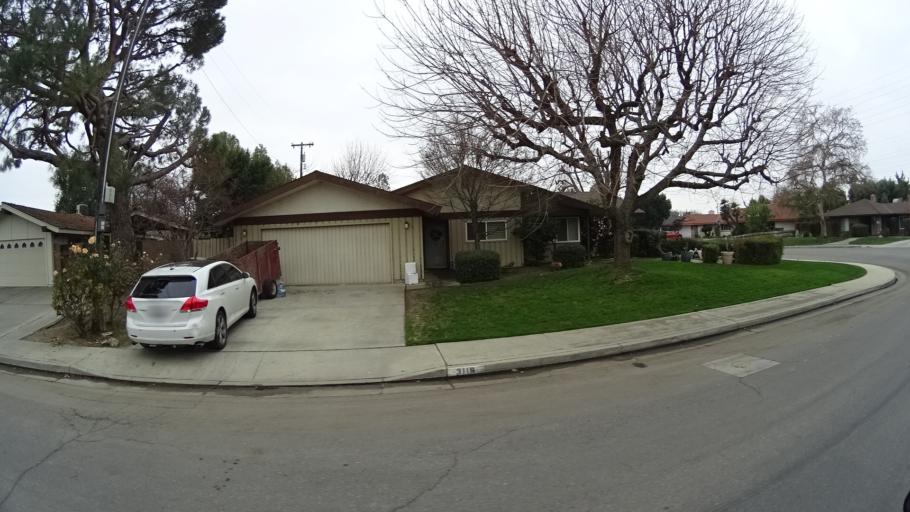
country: US
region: California
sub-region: Kern County
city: Bakersfield
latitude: 35.3838
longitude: -119.0351
